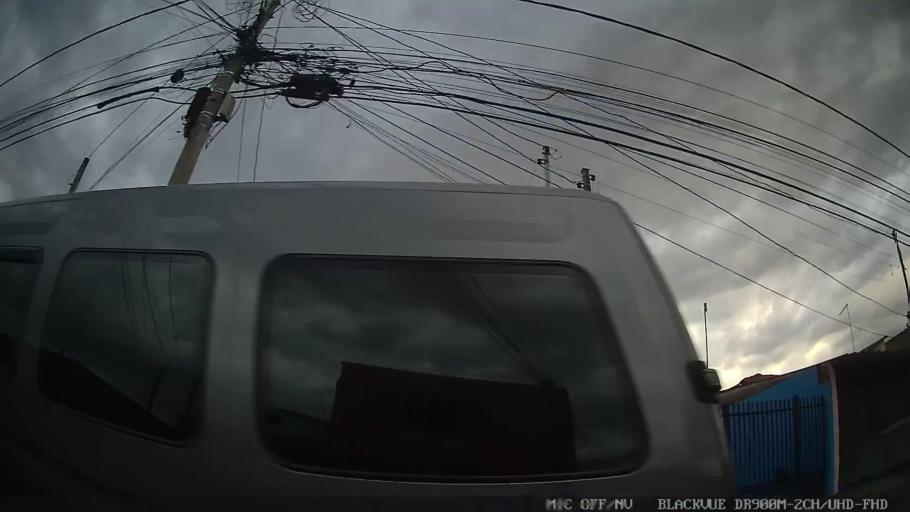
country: BR
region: Sao Paulo
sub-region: Indaiatuba
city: Indaiatuba
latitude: -23.1288
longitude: -47.2443
